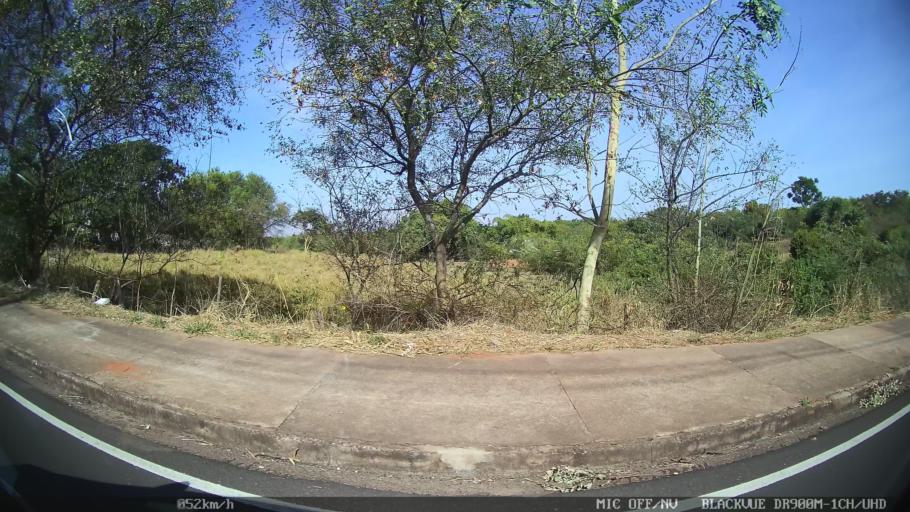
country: BR
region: Sao Paulo
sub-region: Sao Jose Do Rio Preto
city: Sao Jose do Rio Preto
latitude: -20.7890
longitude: -49.4351
